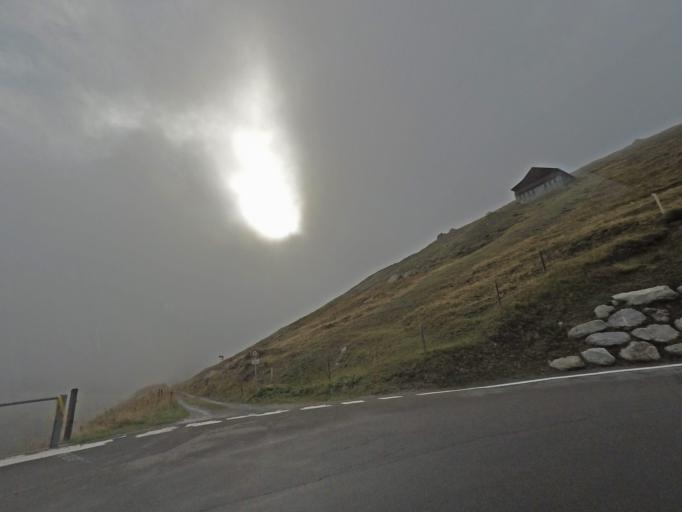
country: CH
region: Uri
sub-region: Uri
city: Andermatt
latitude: 46.5867
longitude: 8.4848
